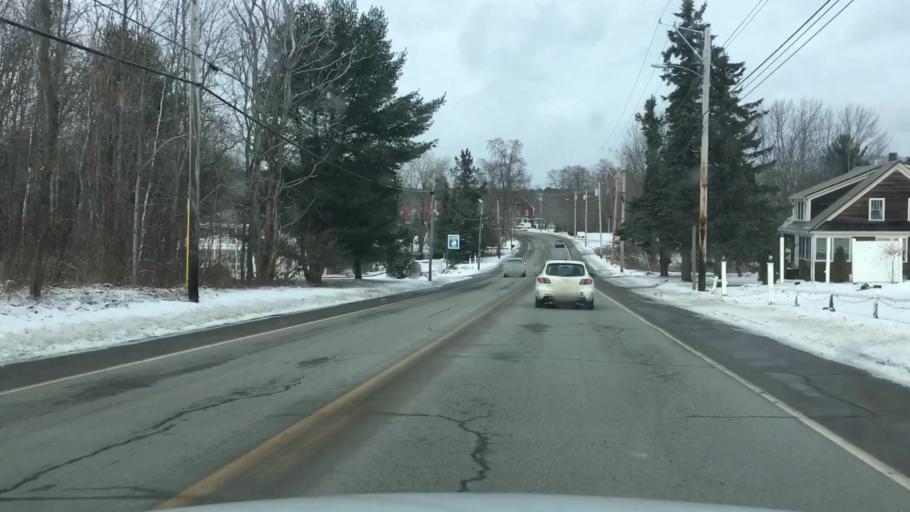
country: US
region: Maine
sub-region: Knox County
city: Rockport
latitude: 44.1774
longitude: -69.0800
